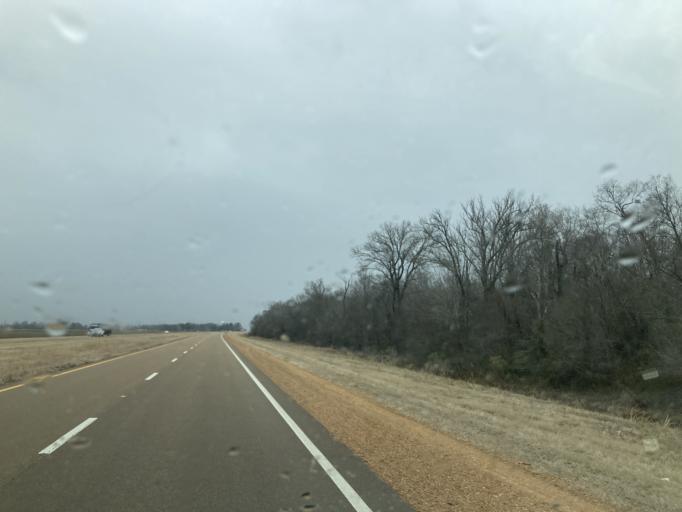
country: US
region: Mississippi
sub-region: Humphreys County
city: Belzoni
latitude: 33.0805
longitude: -90.4818
